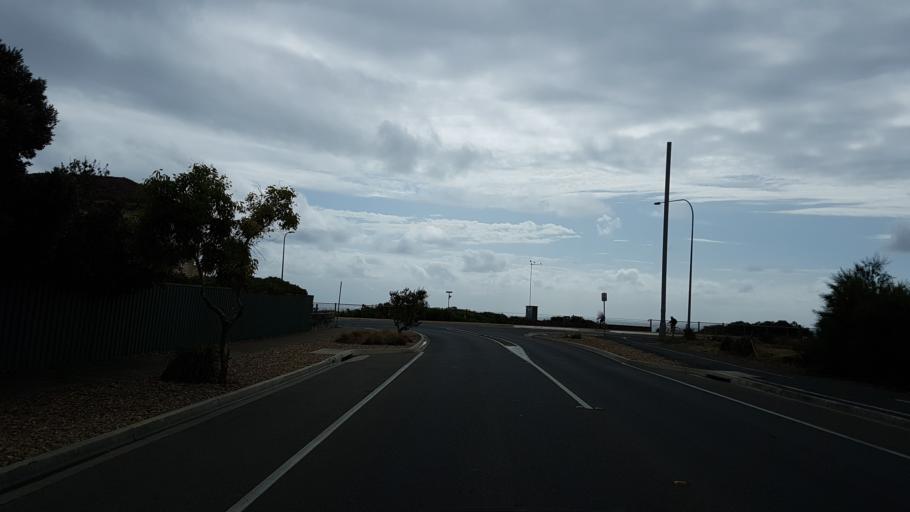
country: AU
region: South Australia
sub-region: Onkaparinga
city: Port Willunga
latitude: -35.2792
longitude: 138.4442
